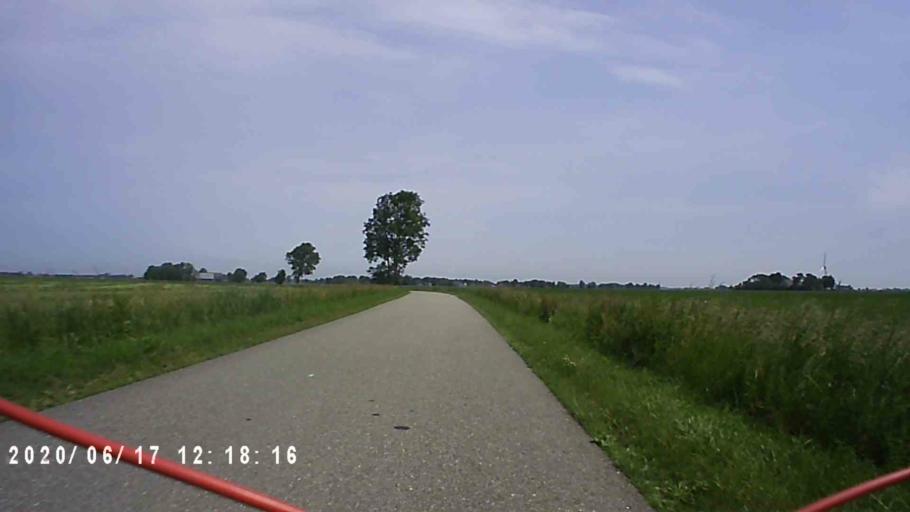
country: NL
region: Groningen
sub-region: Gemeente Zuidhorn
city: Oldehove
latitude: 53.3308
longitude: 6.4147
